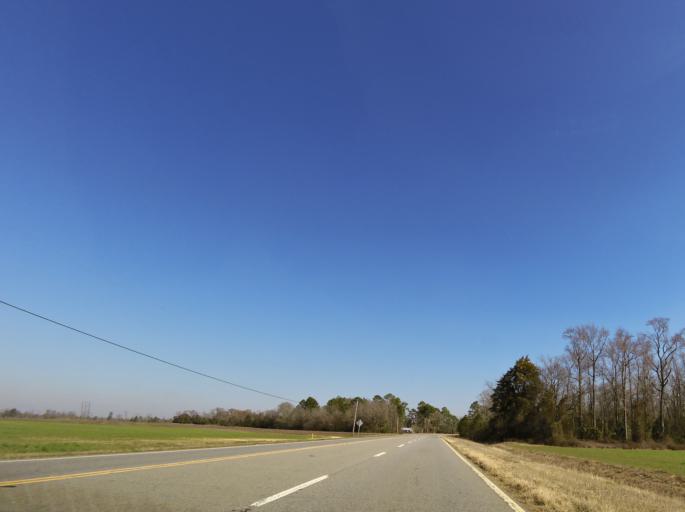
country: US
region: Georgia
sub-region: Bleckley County
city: Cochran
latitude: 32.3562
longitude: -83.3905
